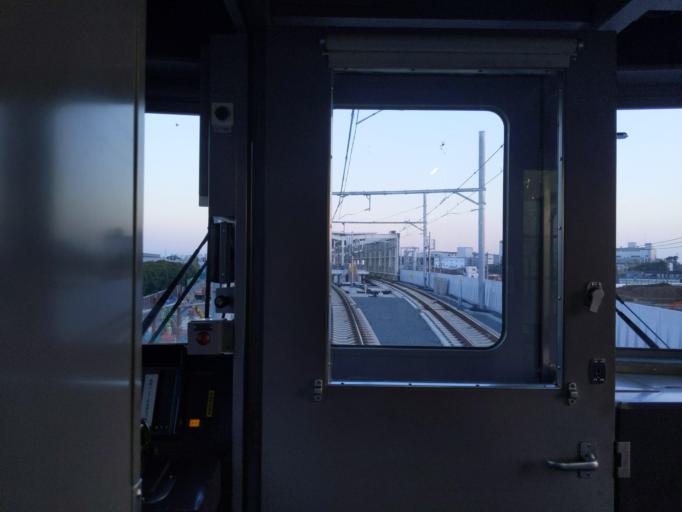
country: JP
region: Chiba
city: Noda
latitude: 35.9448
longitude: 139.8692
